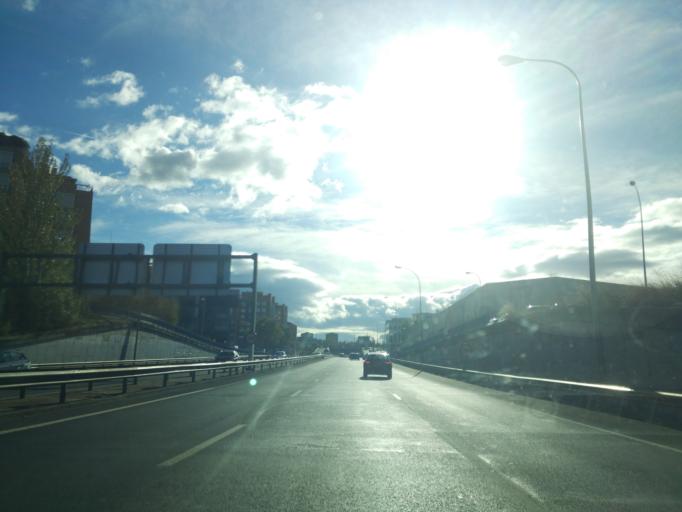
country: ES
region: Madrid
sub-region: Provincia de Madrid
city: Usera
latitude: 40.3803
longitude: -3.6919
